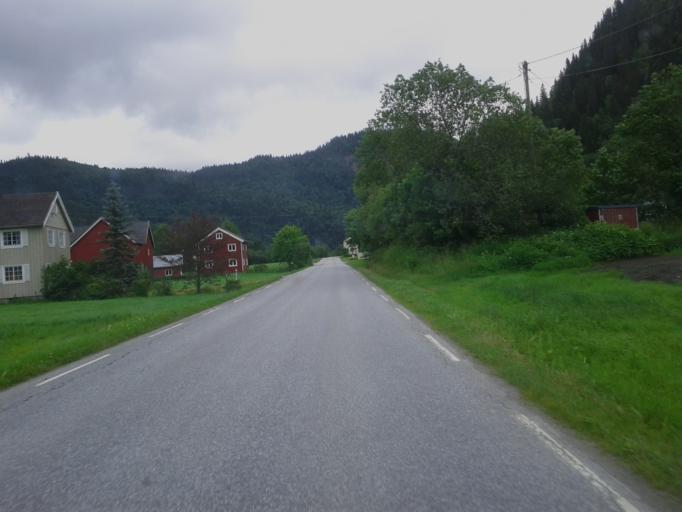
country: NO
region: Sor-Trondelag
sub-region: Midtre Gauldal
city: Storen
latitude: 63.0180
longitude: 10.4189
